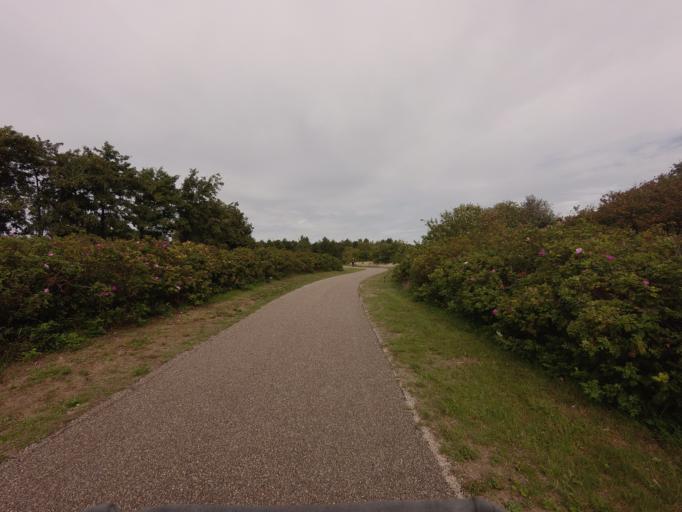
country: NL
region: Friesland
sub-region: Gemeente Ameland
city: Nes
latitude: 53.4513
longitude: 5.7815
